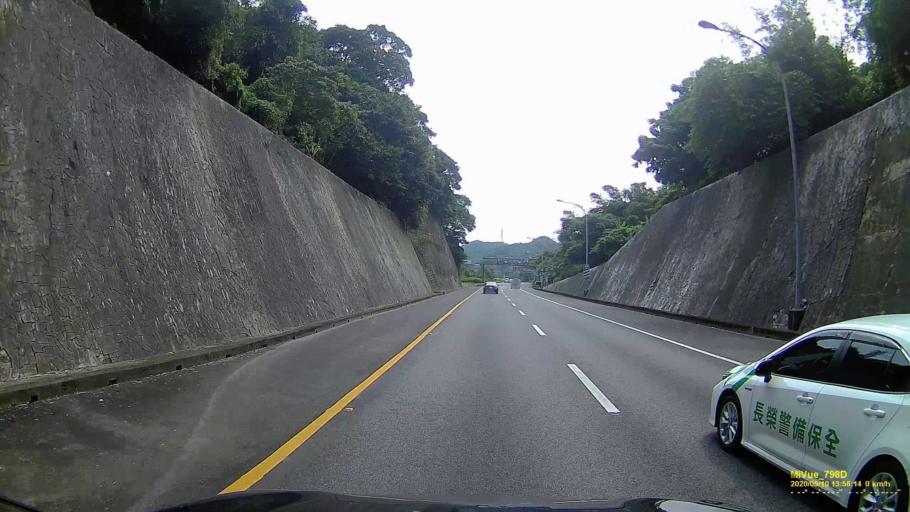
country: TW
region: Taiwan
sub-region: Keelung
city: Keelung
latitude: 25.1200
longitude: 121.7332
